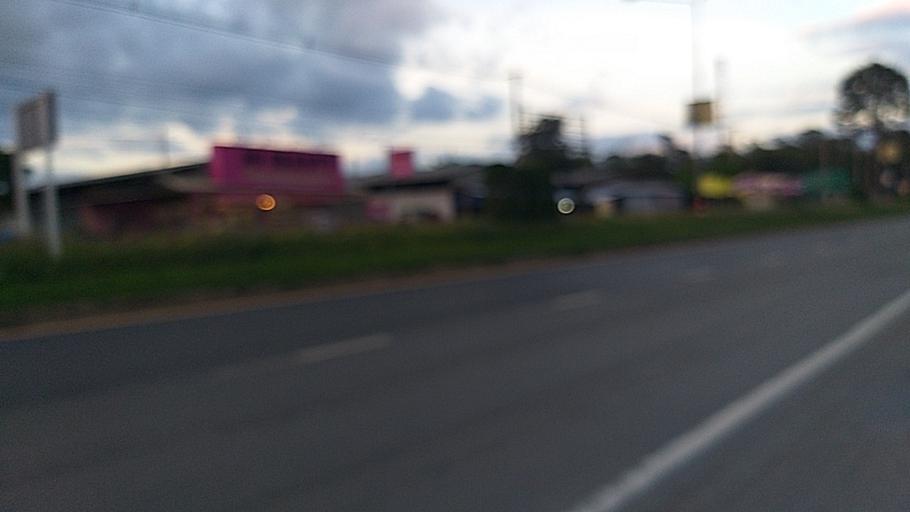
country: TH
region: Surin
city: Kap Choeng
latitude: 14.4524
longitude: 103.6934
